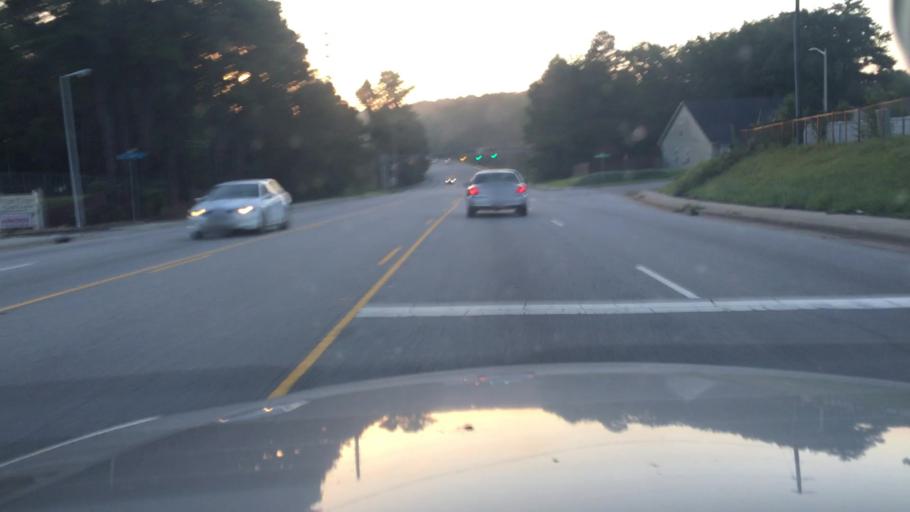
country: US
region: North Carolina
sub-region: Cumberland County
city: Fort Bragg
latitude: 35.0587
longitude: -78.9850
